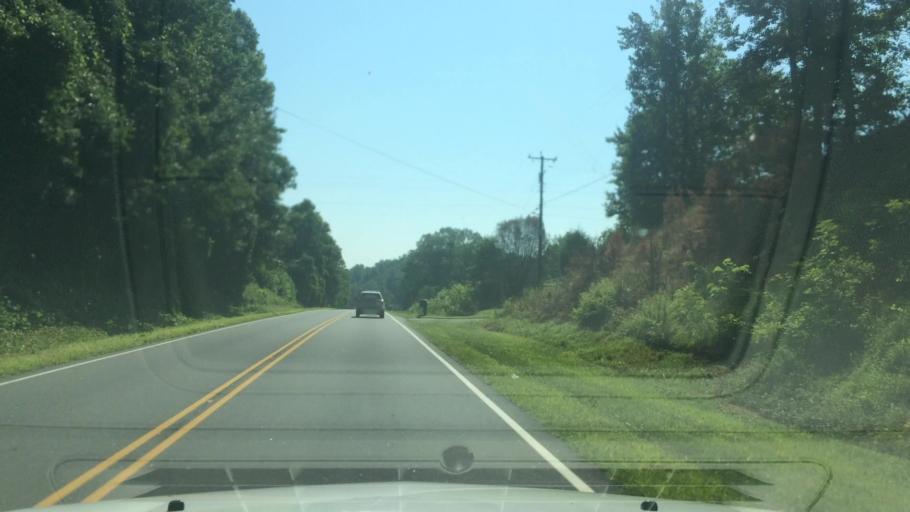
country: US
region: North Carolina
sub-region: Caldwell County
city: Lenoir
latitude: 35.9144
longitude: -81.4762
